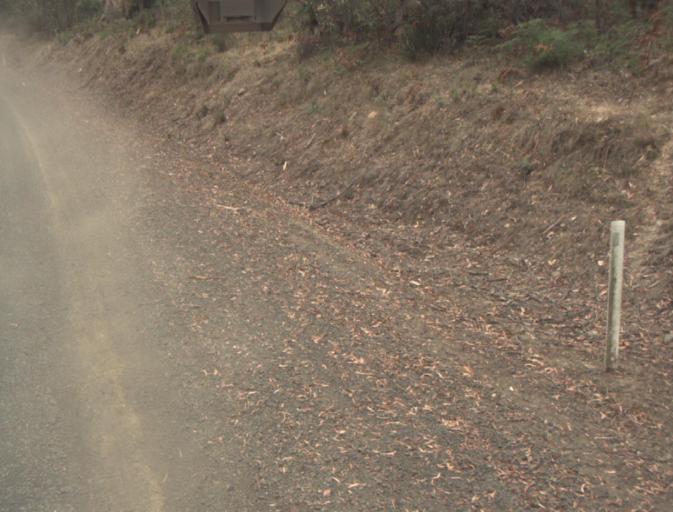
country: AU
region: Tasmania
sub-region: Northern Midlands
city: Evandale
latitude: -41.4843
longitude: 147.5387
